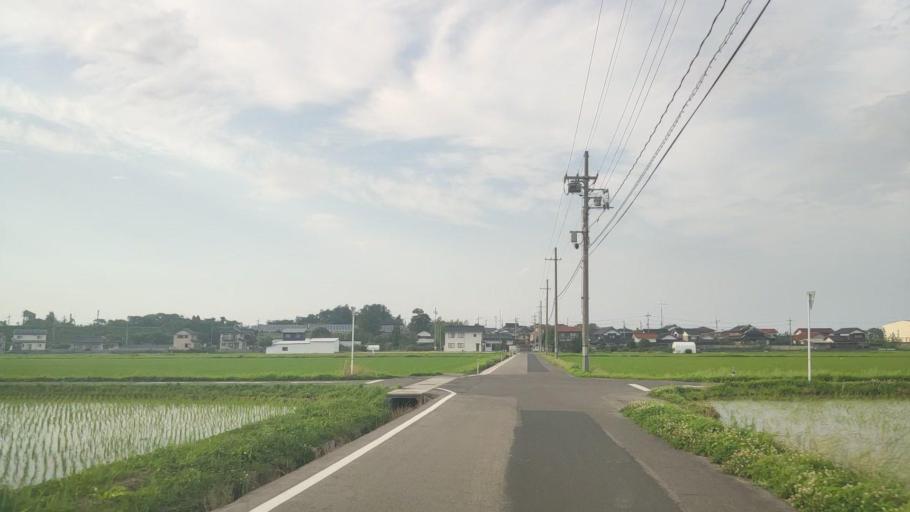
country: JP
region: Tottori
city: Kurayoshi
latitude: 35.4858
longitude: 133.8135
